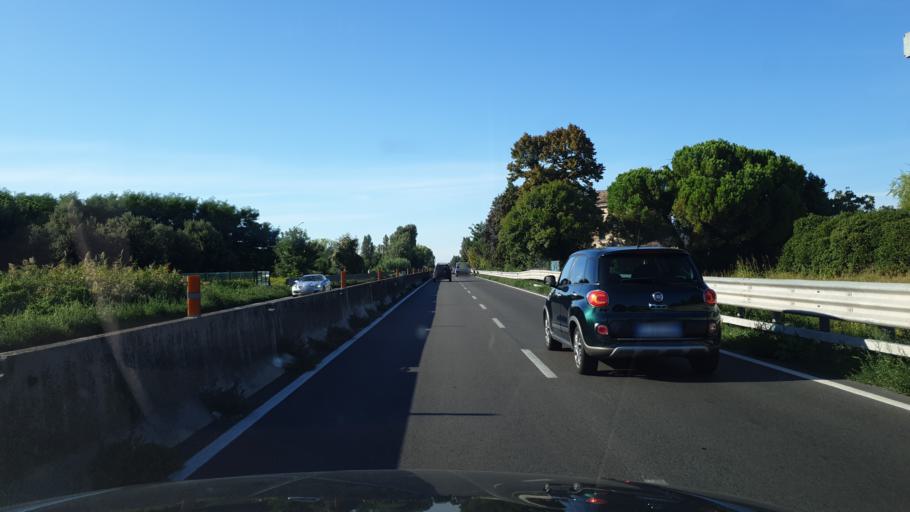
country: IT
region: Emilia-Romagna
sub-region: Provincia di Ravenna
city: Ravenna
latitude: 44.4033
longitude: 12.1779
